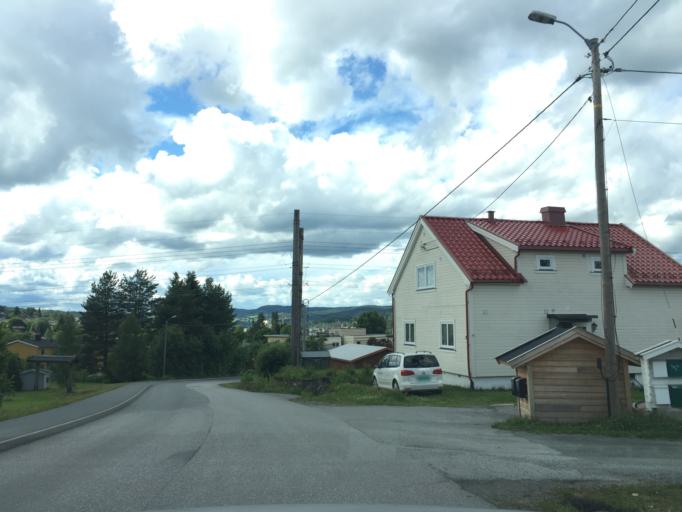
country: NO
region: Hedmark
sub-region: Kongsvinger
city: Kongsvinger
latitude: 60.1823
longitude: 12.0116
